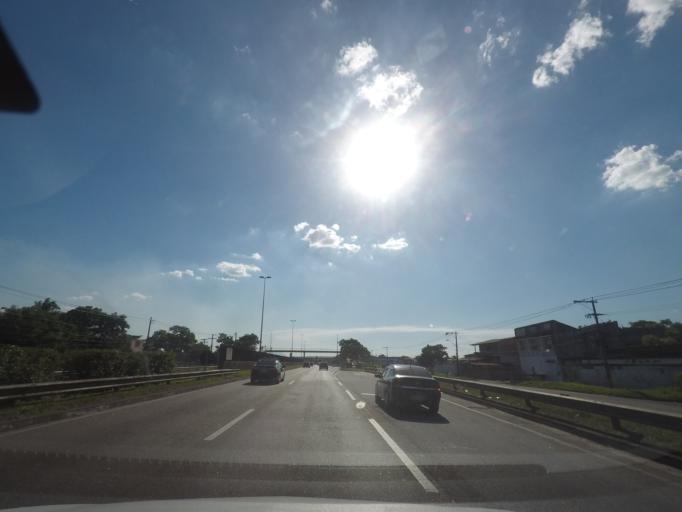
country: BR
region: Rio de Janeiro
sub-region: Duque De Caxias
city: Duque de Caxias
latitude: -22.6507
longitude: -43.2358
